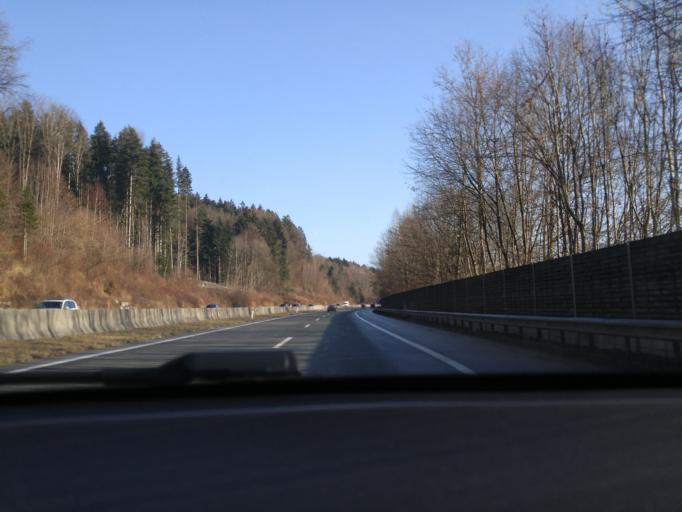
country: AT
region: Salzburg
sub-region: Politischer Bezirk Salzburg-Umgebung
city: Thalgau
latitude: 47.8469
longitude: 13.2480
